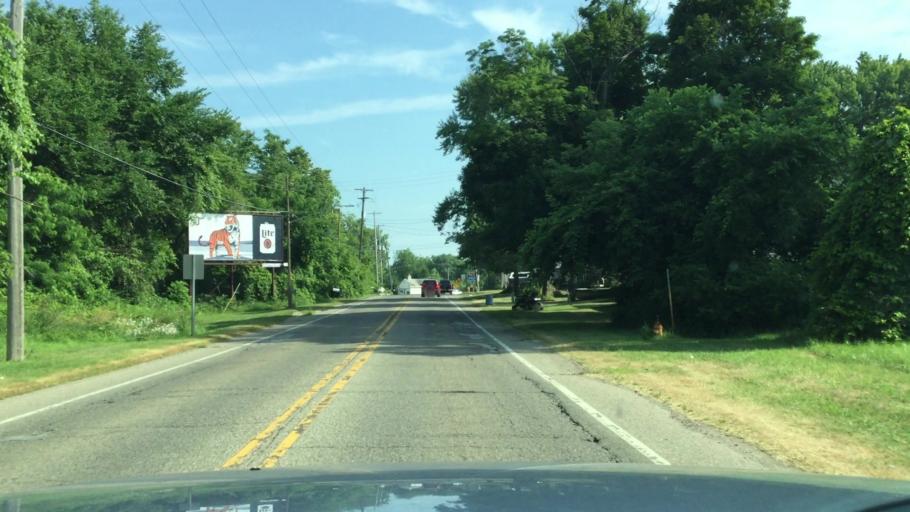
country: US
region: Michigan
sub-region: Genesee County
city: Flushing
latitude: 43.0607
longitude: -83.8625
